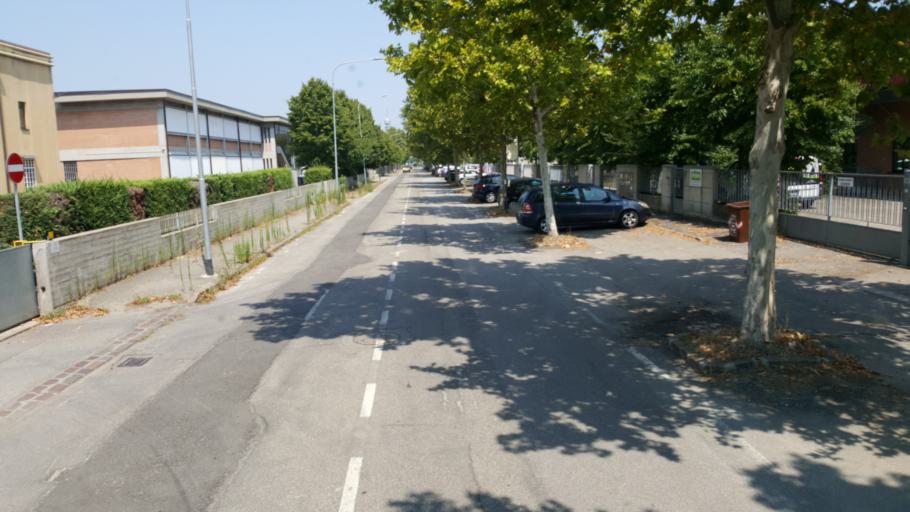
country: IT
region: Emilia-Romagna
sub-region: Provincia di Modena
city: Modena
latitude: 44.6489
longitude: 10.9564
